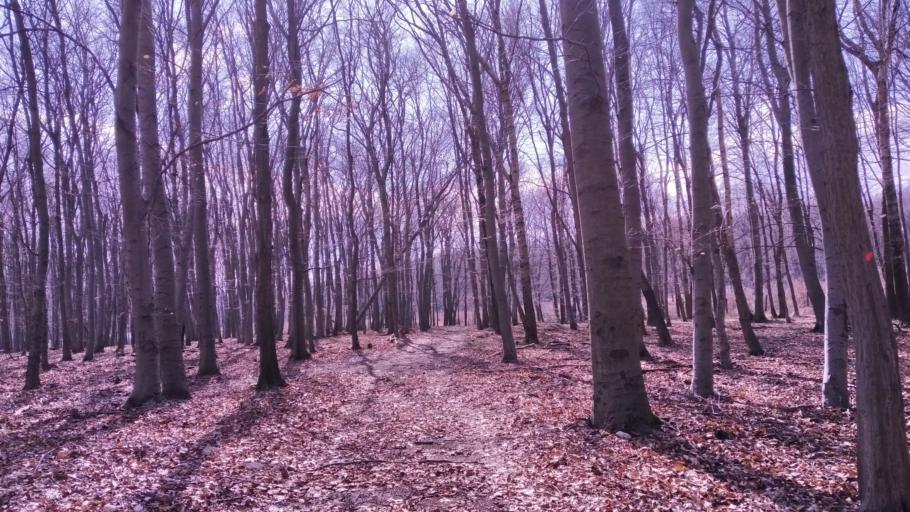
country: HU
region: Komarom-Esztergom
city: Oroszlany
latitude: 47.3987
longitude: 18.3254
